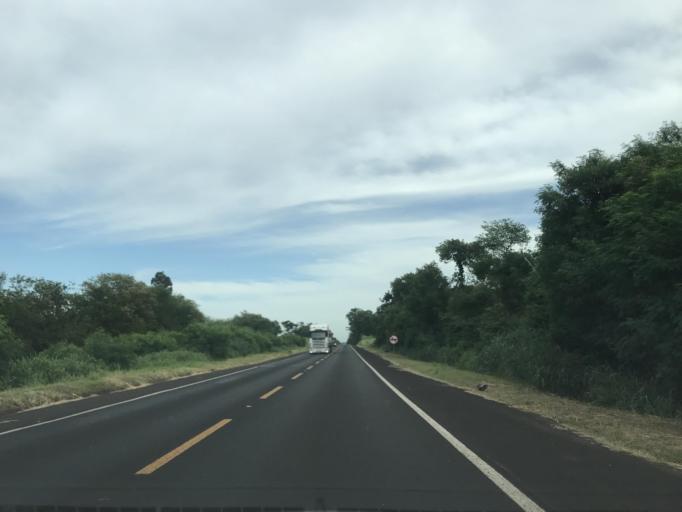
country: BR
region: Parana
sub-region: Paranavai
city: Paranavai
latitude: -23.0243
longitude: -52.4906
